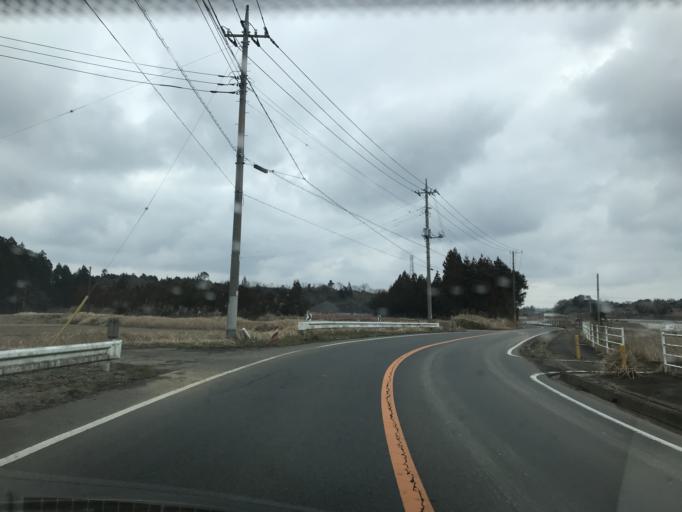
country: JP
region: Chiba
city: Sawara
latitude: 35.8313
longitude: 140.5040
